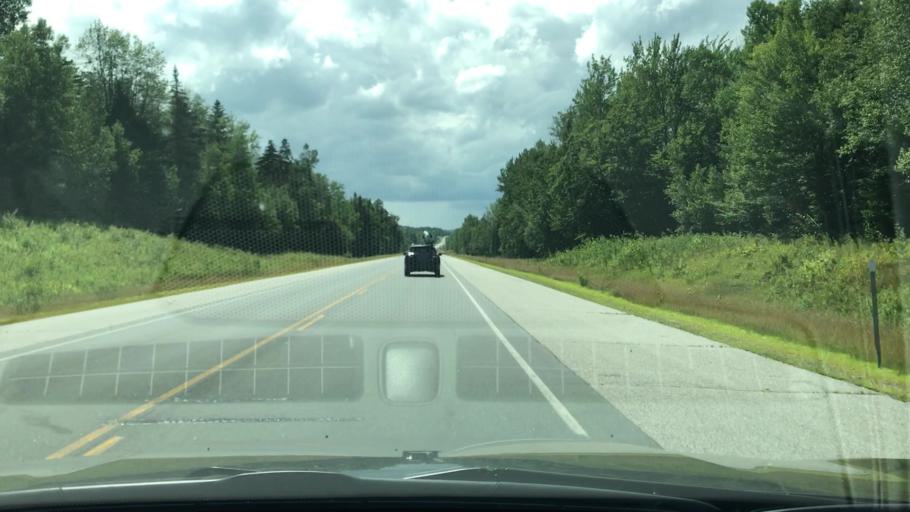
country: US
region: New Hampshire
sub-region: Coos County
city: Jefferson
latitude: 44.3668
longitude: -71.4529
